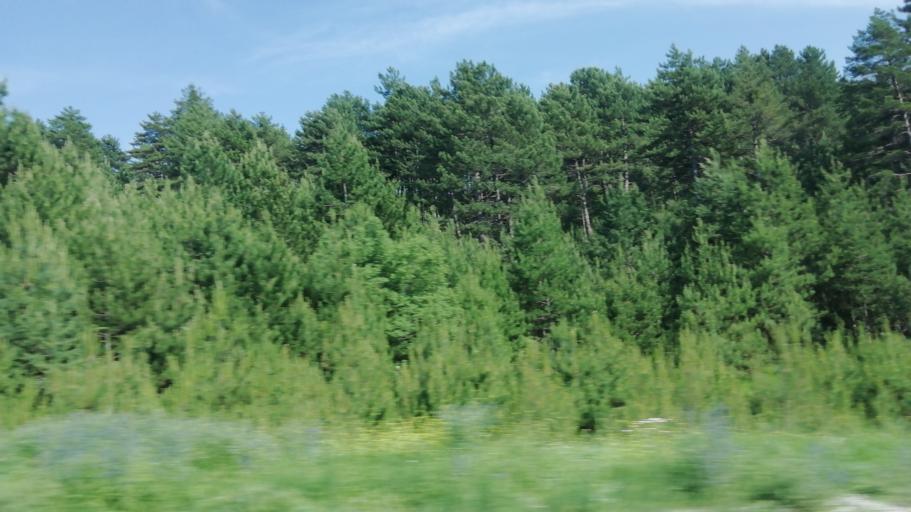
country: TR
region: Karabuk
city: Karabuk
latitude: 41.1218
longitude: 32.5847
